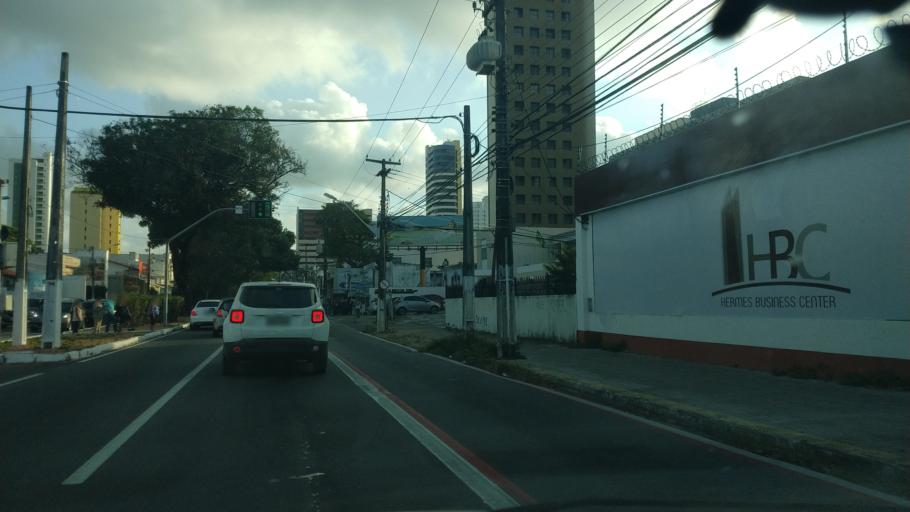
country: BR
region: Rio Grande do Norte
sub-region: Natal
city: Natal
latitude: -5.7968
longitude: -35.1993
